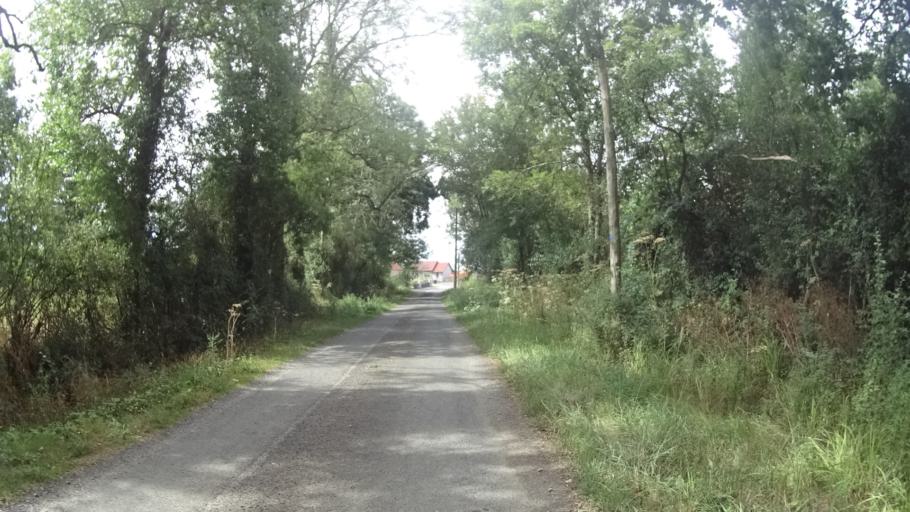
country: FR
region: Auvergne
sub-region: Departement de l'Allier
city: Beaulon
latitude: 46.6462
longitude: 3.6693
